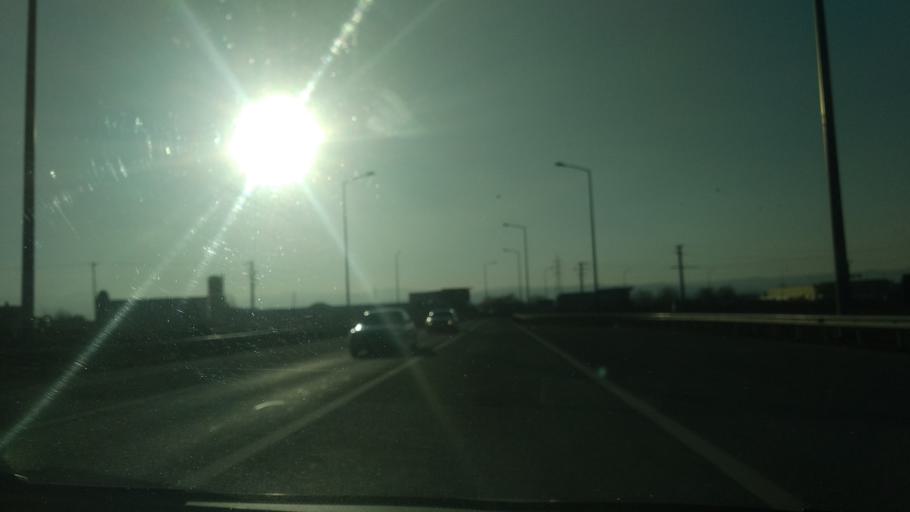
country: XK
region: Pristina
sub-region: Lipjan
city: Lipljan
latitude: 42.5448
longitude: 21.1283
